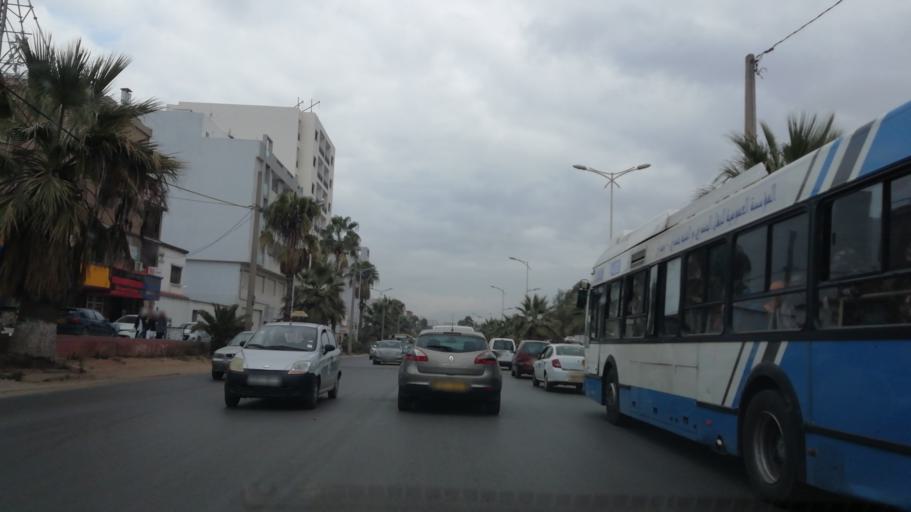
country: DZ
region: Oran
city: Oran
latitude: 35.6914
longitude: -0.6197
